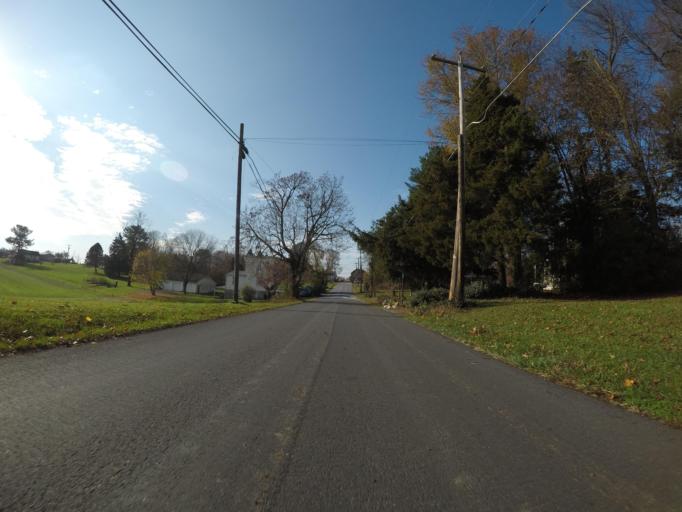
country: US
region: Maryland
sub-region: Carroll County
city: Hampstead
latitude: 39.5431
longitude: -76.8314
